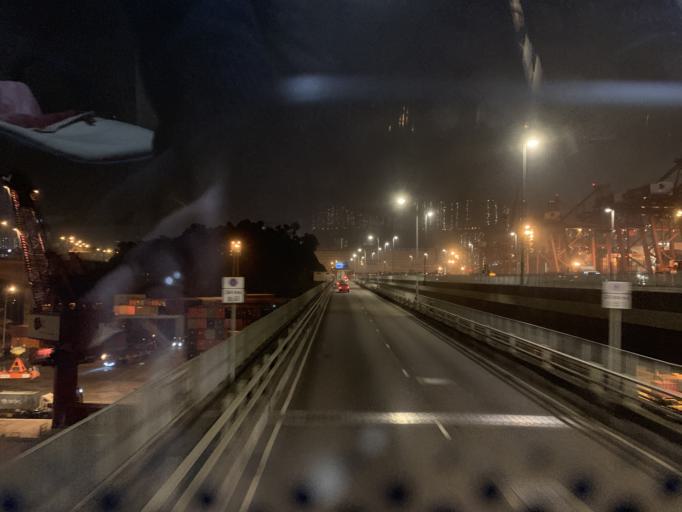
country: HK
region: Tsuen Wan
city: Tsuen Wan
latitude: 22.3488
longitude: 114.1143
